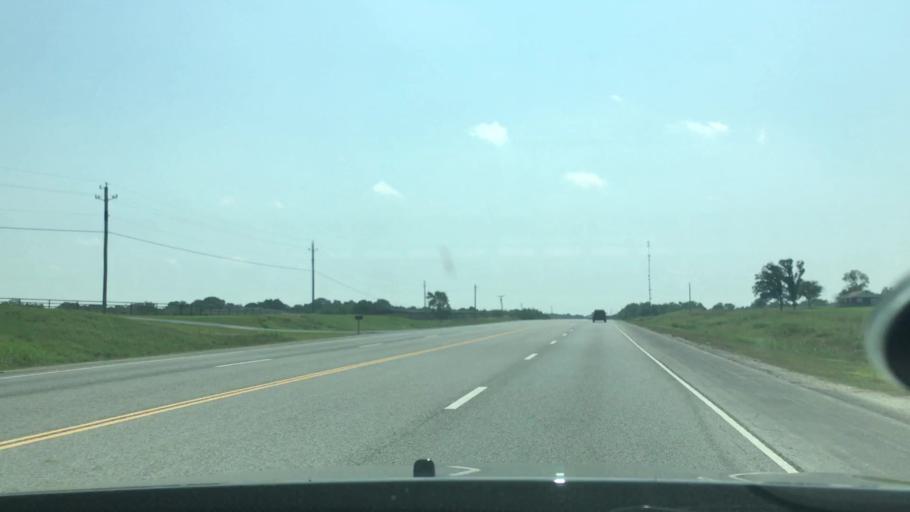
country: US
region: Oklahoma
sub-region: Atoka County
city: Atoka
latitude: 34.3648
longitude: -96.1002
